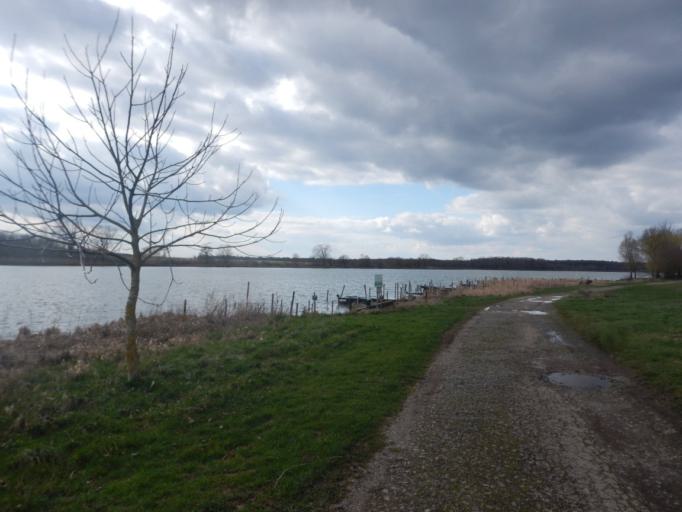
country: FR
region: Lorraine
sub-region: Departement de la Moselle
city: Lorquin
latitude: 48.6922
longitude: 6.9229
